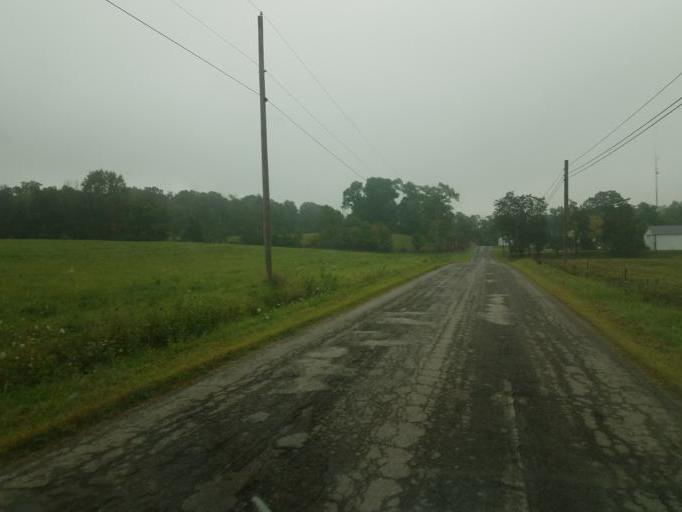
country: US
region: Ohio
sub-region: Morrow County
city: Mount Gilead
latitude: 40.5356
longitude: -82.7369
